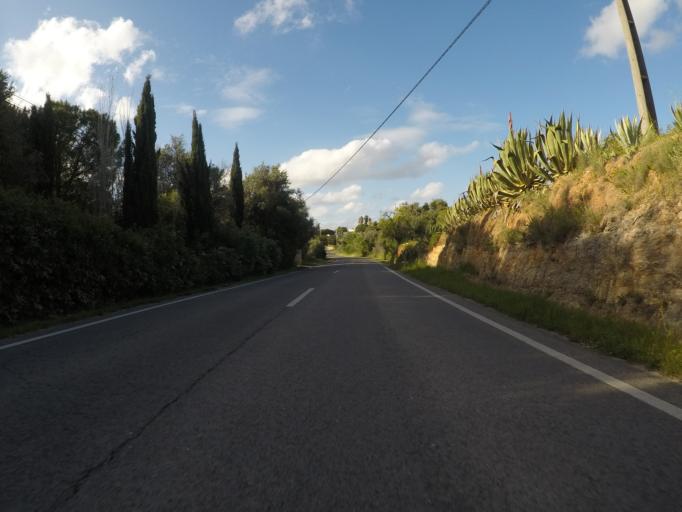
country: PT
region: Faro
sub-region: Lagoa
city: Carvoeiro
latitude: 37.1083
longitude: -8.4461
